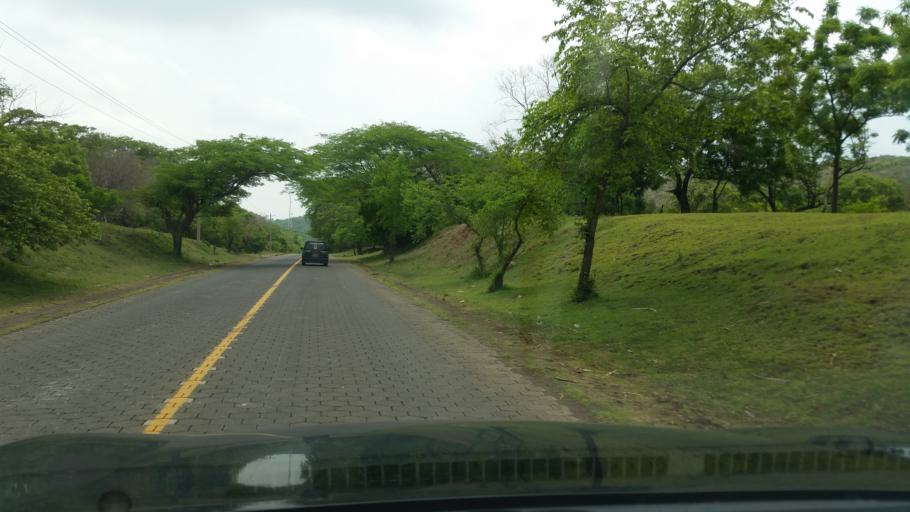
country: NI
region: Managua
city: Masachapa
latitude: 11.8512
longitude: -86.5175
